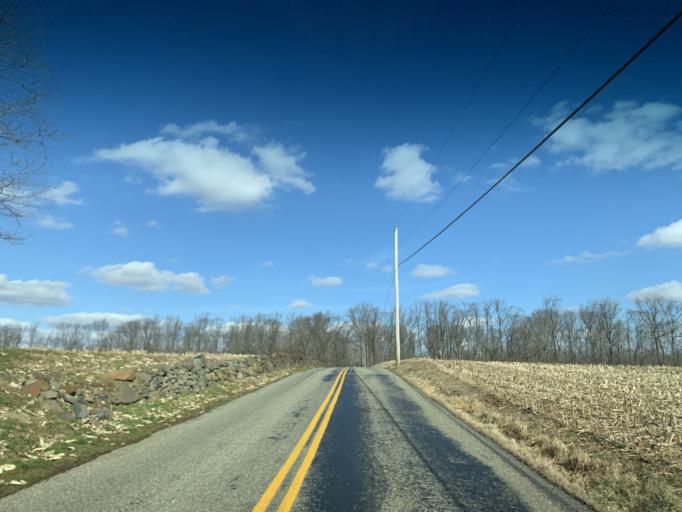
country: US
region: Maryland
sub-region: Harford County
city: Aberdeen
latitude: 39.5421
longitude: -76.2119
